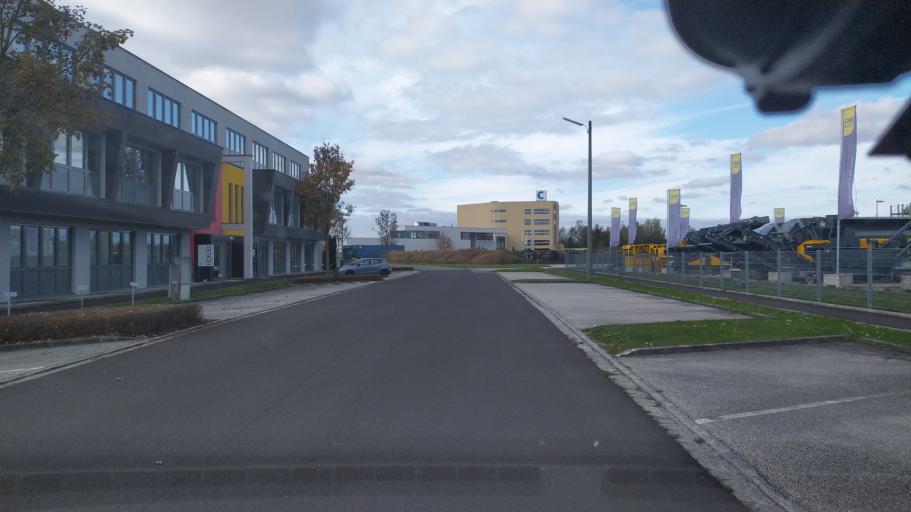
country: AT
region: Upper Austria
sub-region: Politischer Bezirk Urfahr-Umgebung
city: Steyregg
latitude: 48.2541
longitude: 14.3782
